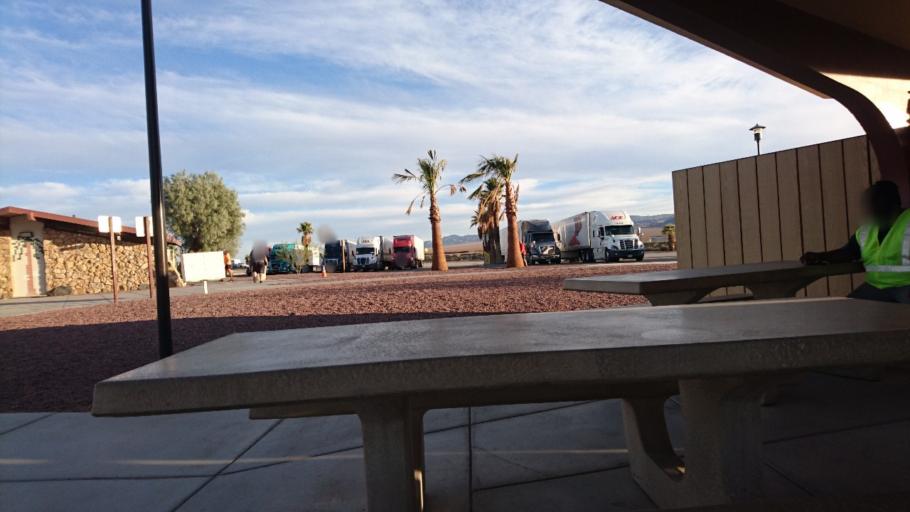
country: US
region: California
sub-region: San Bernardino County
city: Fort Irwin
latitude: 34.8017
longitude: -116.5216
